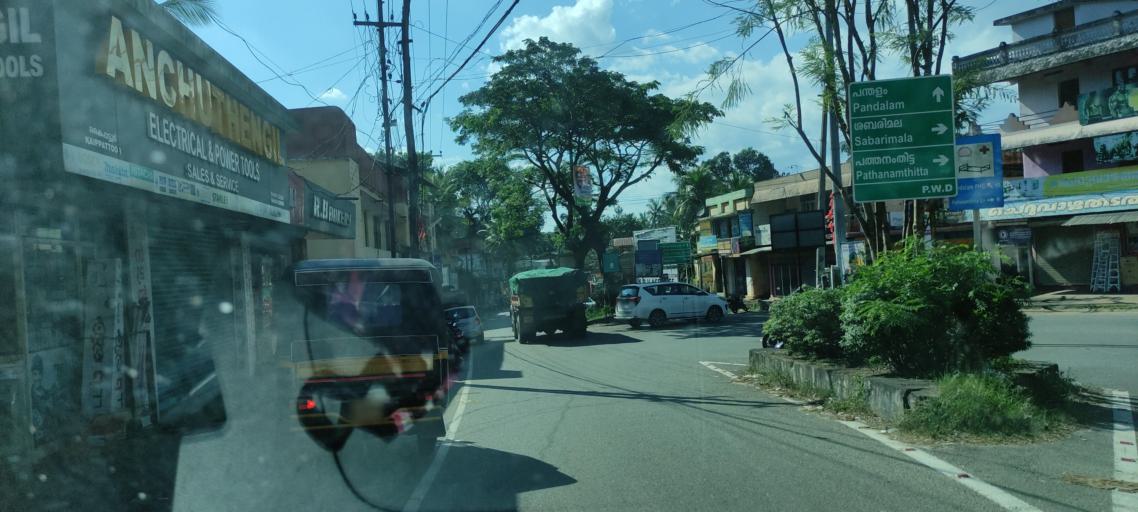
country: IN
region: Kerala
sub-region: Pattanamtitta
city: Pathanamthitta
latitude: 9.2313
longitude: 76.7507
